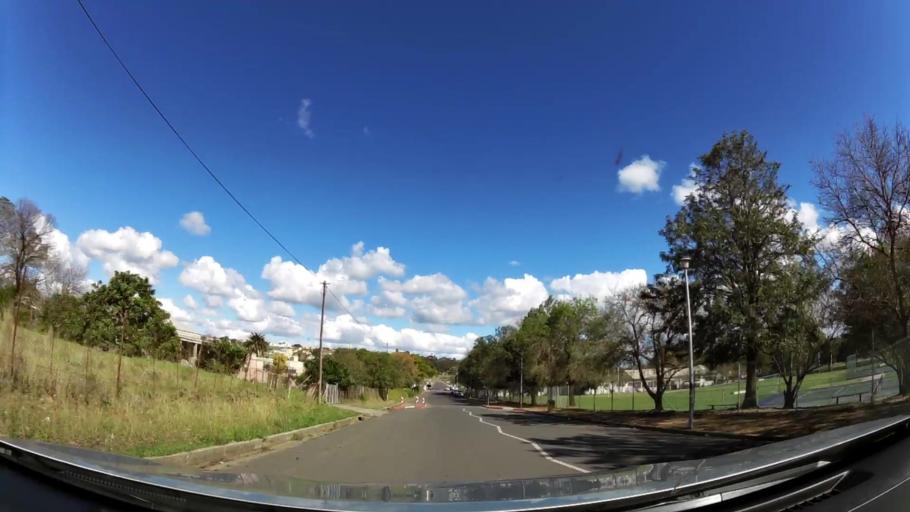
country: ZA
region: Western Cape
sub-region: Overberg District Municipality
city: Swellendam
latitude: -34.0261
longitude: 20.4449
